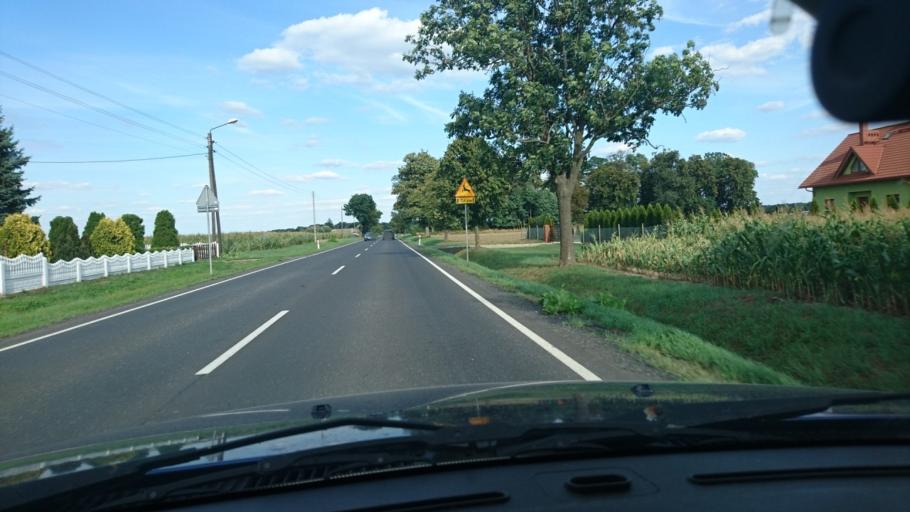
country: PL
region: Greater Poland Voivodeship
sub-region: Powiat krotoszynski
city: Kobylin
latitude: 51.7302
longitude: 17.2828
